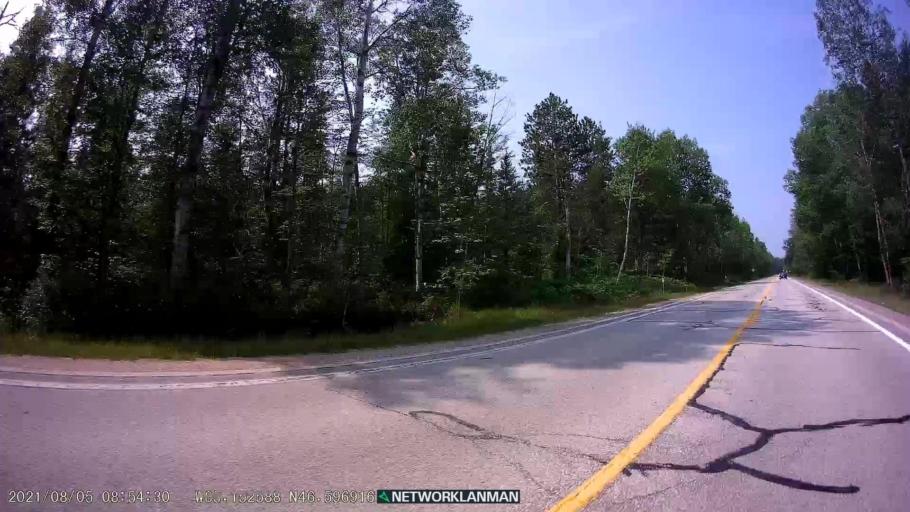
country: US
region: Michigan
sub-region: Luce County
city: Newberry
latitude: 46.5970
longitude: -85.1538
